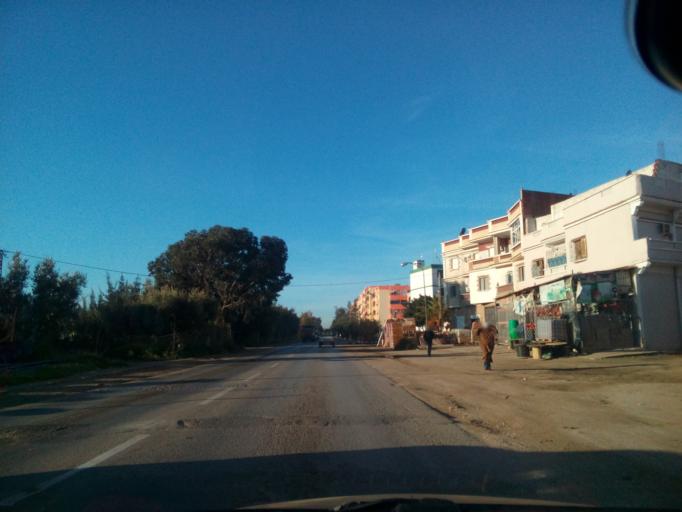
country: DZ
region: Relizane
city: Relizane
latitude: 35.7200
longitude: 0.3605
